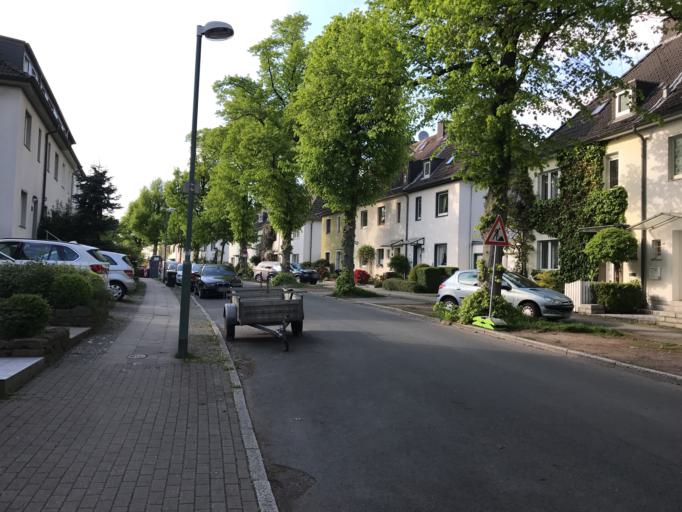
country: DE
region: North Rhine-Westphalia
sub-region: Regierungsbezirk Dusseldorf
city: Essen
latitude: 51.4215
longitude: 7.0318
